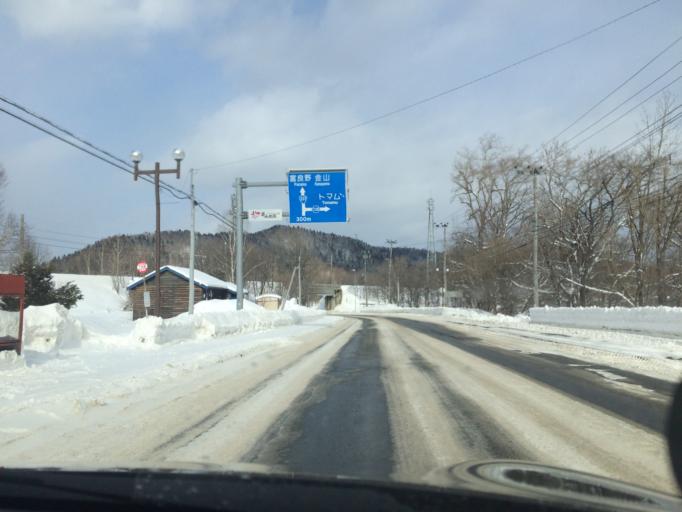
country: JP
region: Hokkaido
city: Shimo-furano
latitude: 43.0017
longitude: 142.4065
